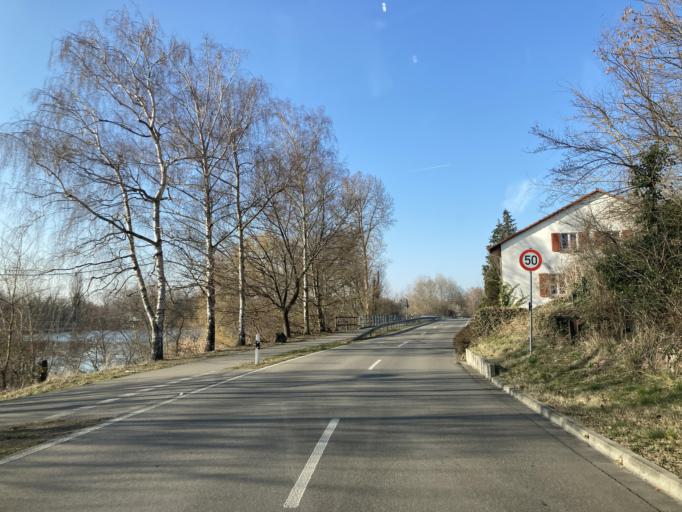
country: DE
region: Baden-Wuerttemberg
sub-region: Freiburg Region
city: Sasbach
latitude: 48.1488
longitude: 7.6010
